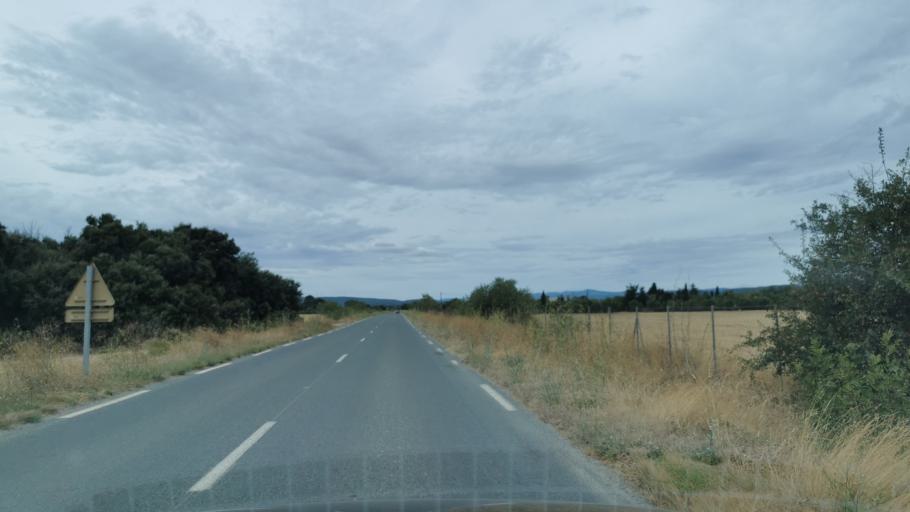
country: FR
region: Languedoc-Roussillon
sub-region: Departement de l'Aude
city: Argeliers
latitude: 43.2857
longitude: 2.9117
